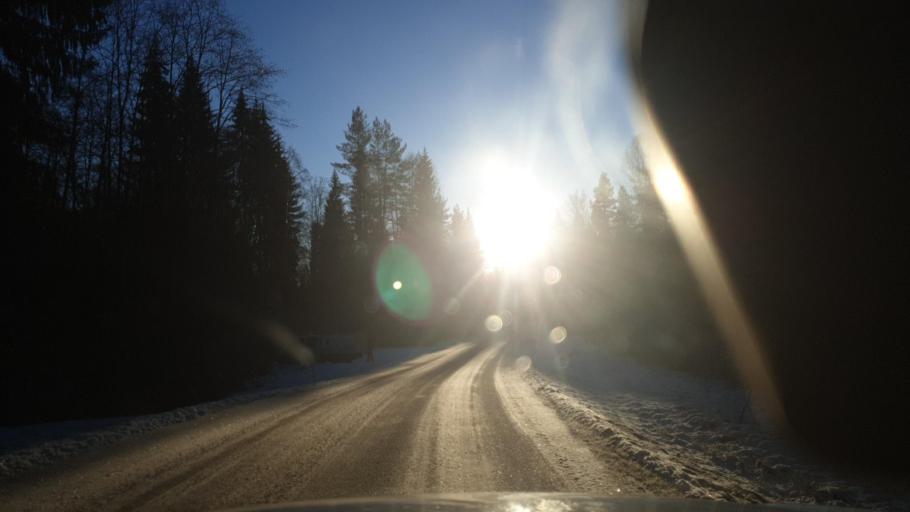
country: SE
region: Vaermland
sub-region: Arvika Kommun
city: Arvika
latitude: 59.7898
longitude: 12.8393
